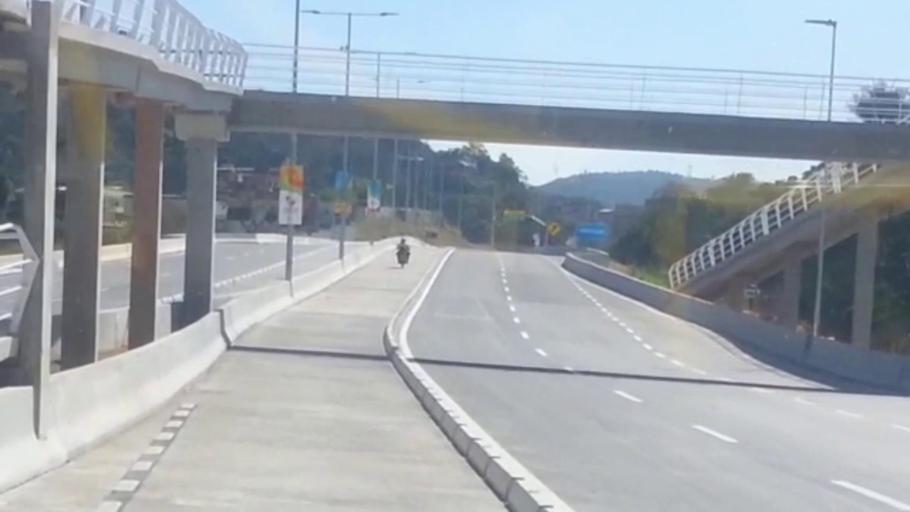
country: BR
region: Rio de Janeiro
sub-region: Nilopolis
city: Nilopolis
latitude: -22.9272
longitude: -43.3961
